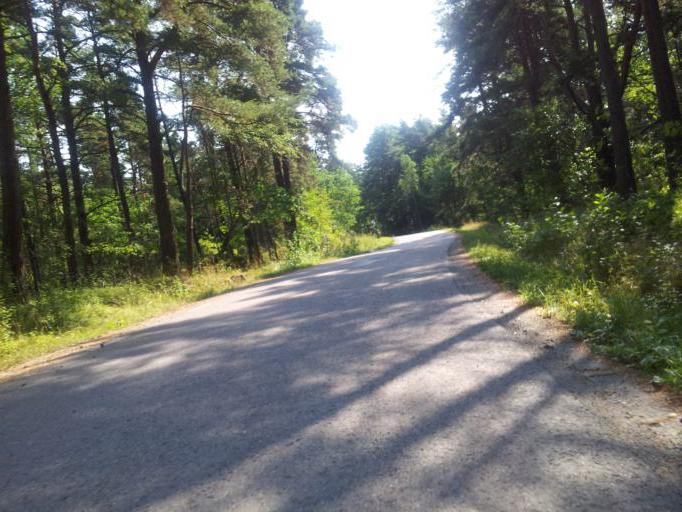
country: SE
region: Uppsala
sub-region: Uppsala Kommun
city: Gamla Uppsala
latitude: 59.8993
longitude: 17.6720
